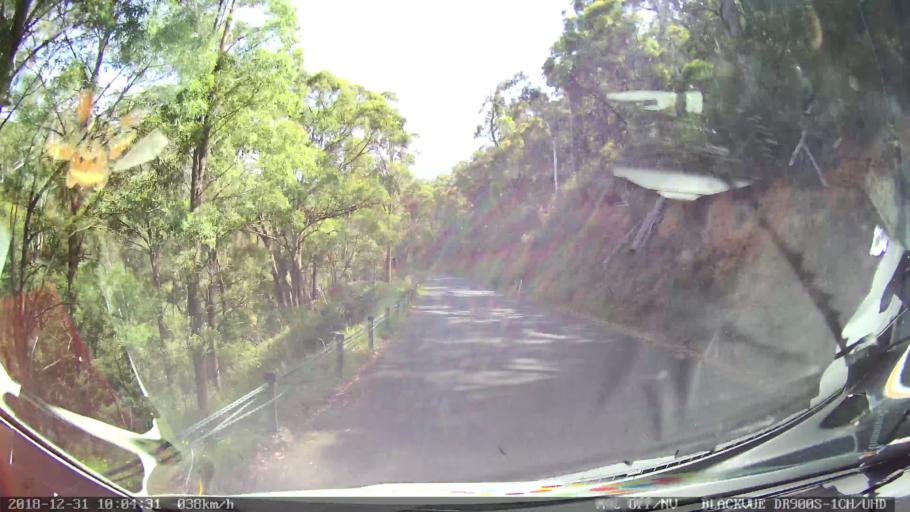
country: AU
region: New South Wales
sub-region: Snowy River
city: Jindabyne
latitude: -36.5311
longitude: 148.1918
